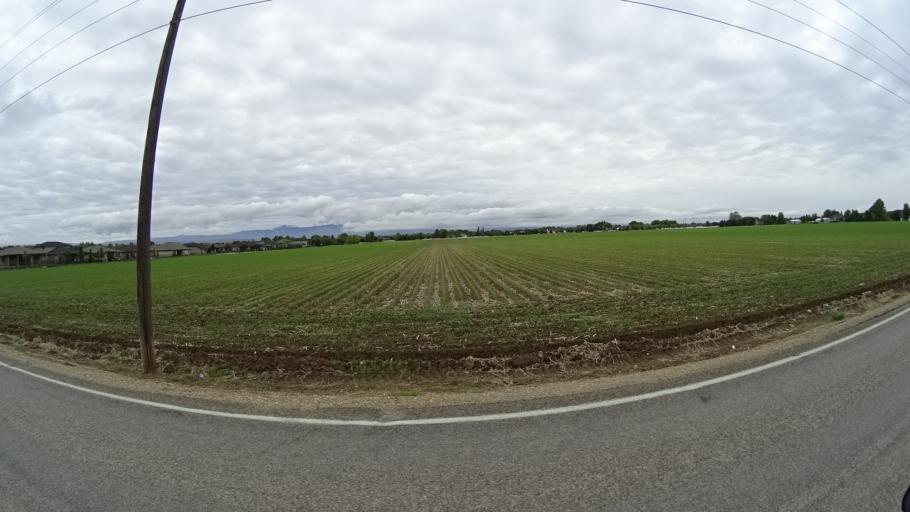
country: US
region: Idaho
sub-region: Ada County
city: Eagle
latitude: 43.7090
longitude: -116.4138
